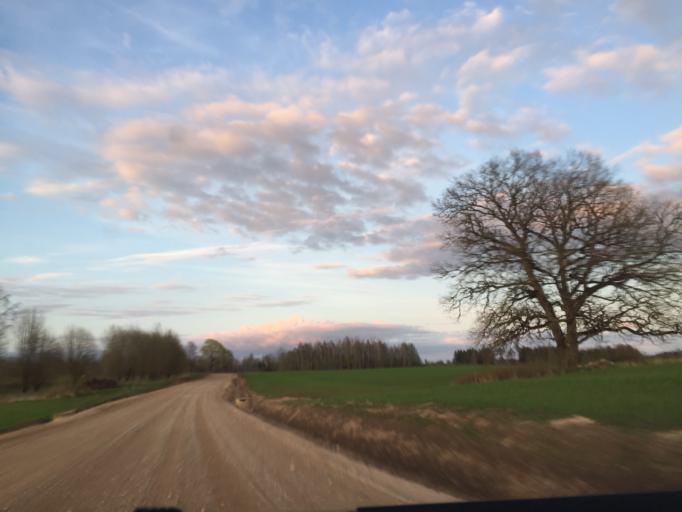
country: LV
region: Gulbenes Rajons
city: Gulbene
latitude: 57.2511
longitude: 26.9011
